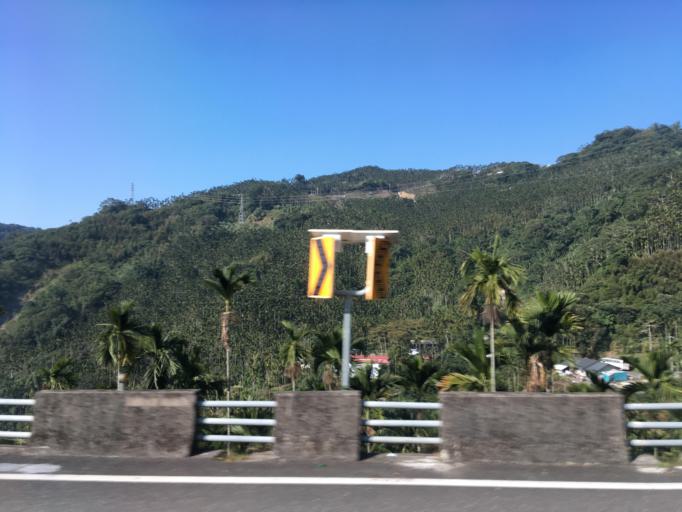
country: TW
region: Taiwan
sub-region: Chiayi
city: Jiayi Shi
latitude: 23.4331
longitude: 120.6386
